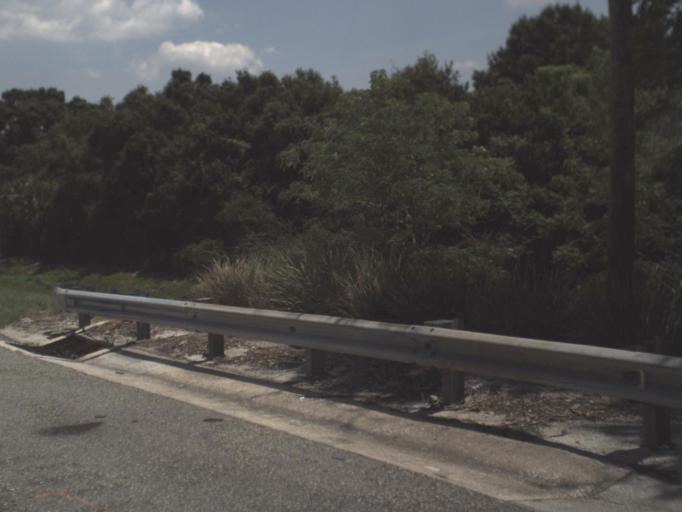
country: US
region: Florida
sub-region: Pinellas County
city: Lealman
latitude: 27.8308
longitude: -82.6660
